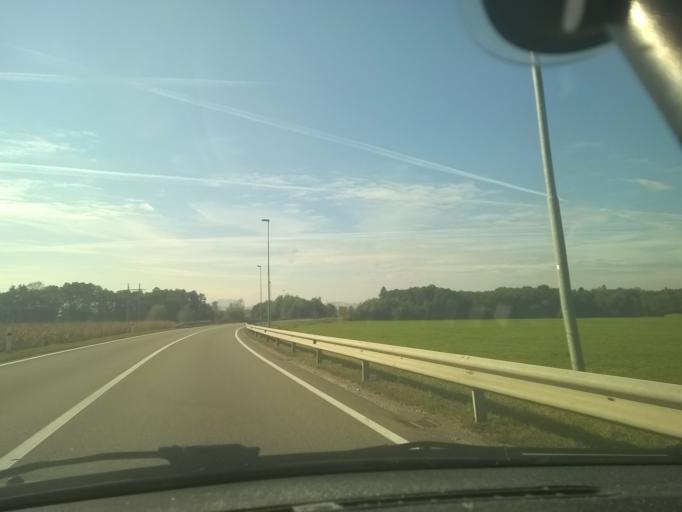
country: SI
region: Ptuj
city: Ptuj
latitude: 46.4003
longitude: 15.8755
